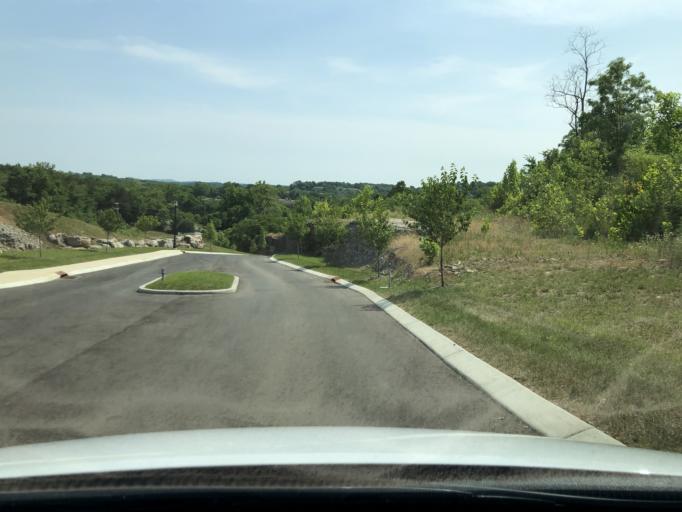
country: US
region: Tennessee
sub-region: Rutherford County
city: La Vergne
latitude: 36.0614
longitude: -86.6702
